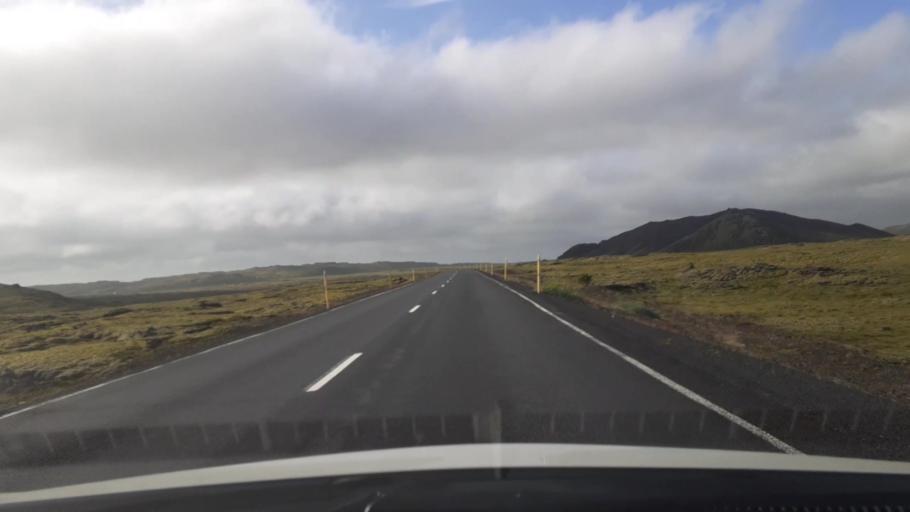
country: IS
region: South
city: THorlakshoefn
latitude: 63.9705
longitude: -21.4582
